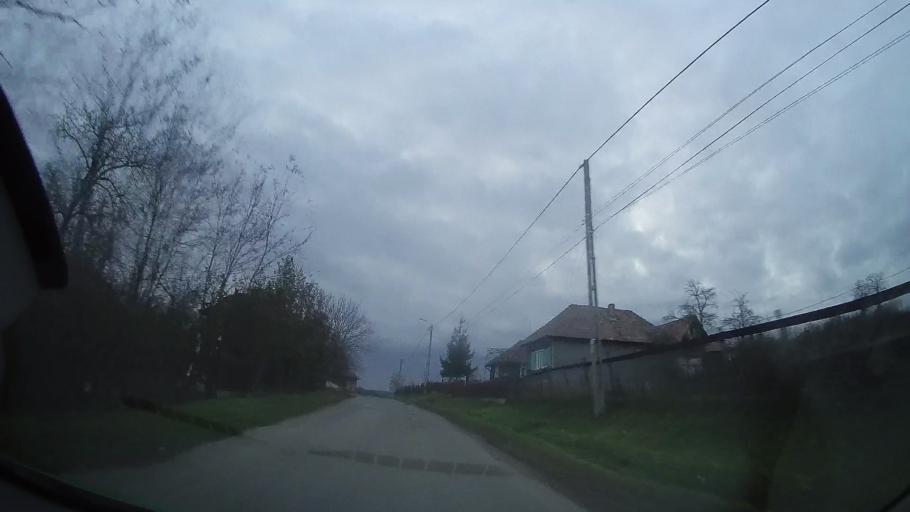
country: RO
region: Cluj
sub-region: Comuna Caianu
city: Vaida-Camaras
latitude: 46.8308
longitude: 23.9538
